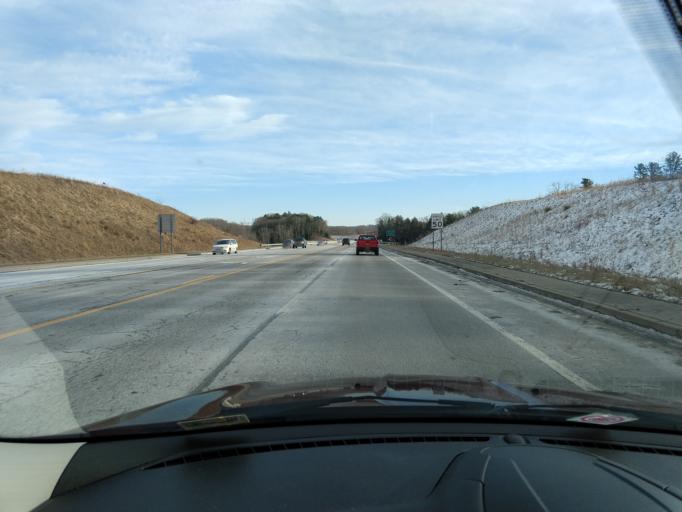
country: US
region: West Virginia
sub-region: Raleigh County
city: Stanaford
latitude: 37.7885
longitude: -81.1587
